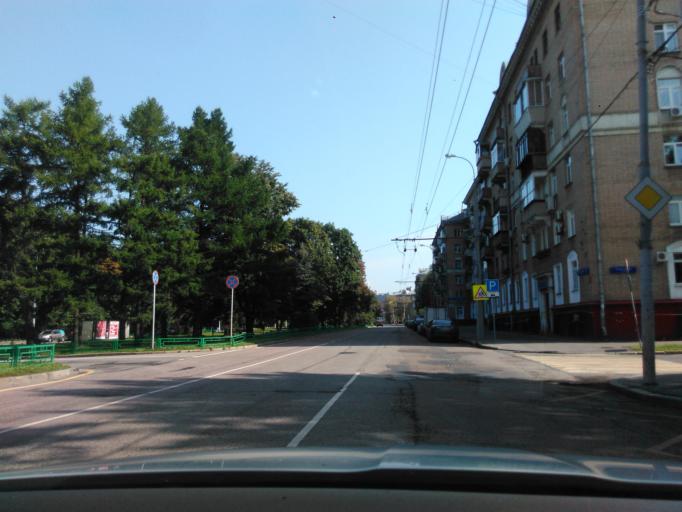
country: RU
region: Moscow
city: Sokol
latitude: 55.7967
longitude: 37.5135
